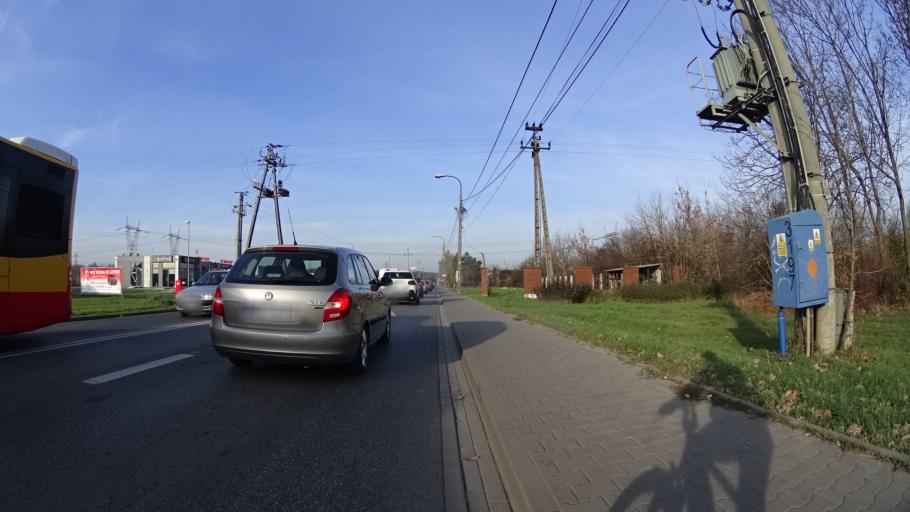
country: PL
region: Masovian Voivodeship
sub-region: Powiat warszawski zachodni
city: Babice
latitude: 52.2883
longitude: 20.8767
